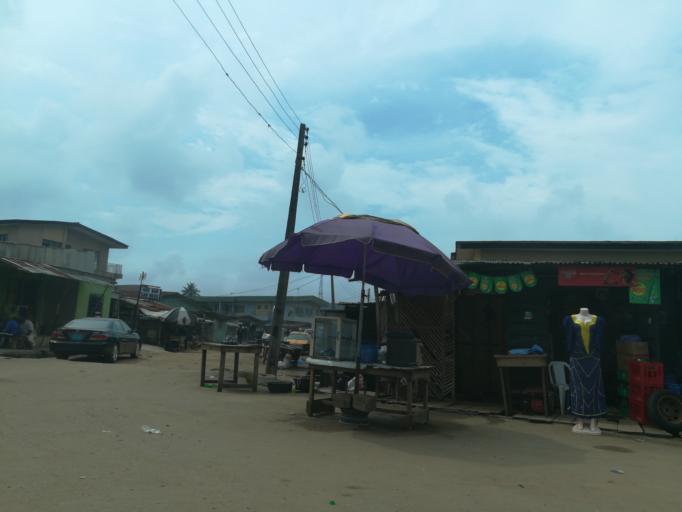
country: NG
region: Lagos
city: Ikorodu
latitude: 6.6201
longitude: 3.5087
